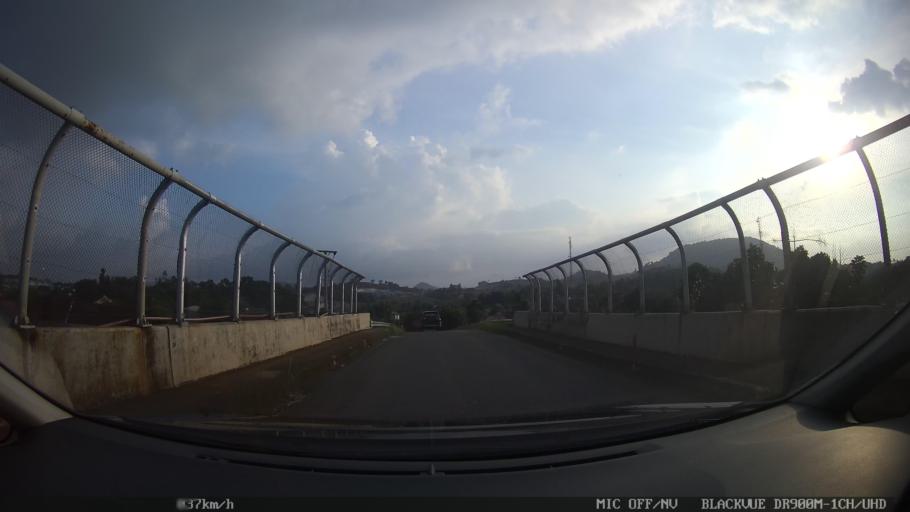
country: ID
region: Lampung
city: Panjang
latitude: -5.4000
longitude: 105.3531
